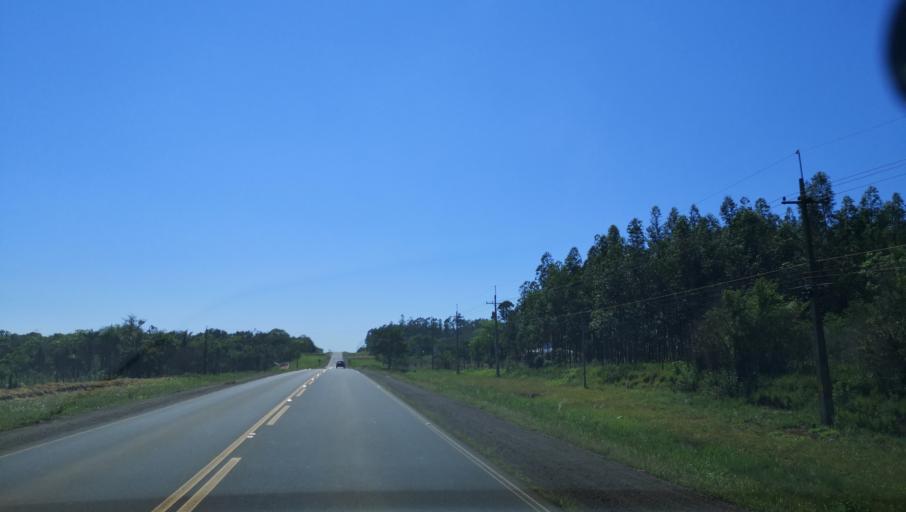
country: PY
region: Itapua
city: Carmen del Parana
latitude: -27.2197
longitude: -56.0993
